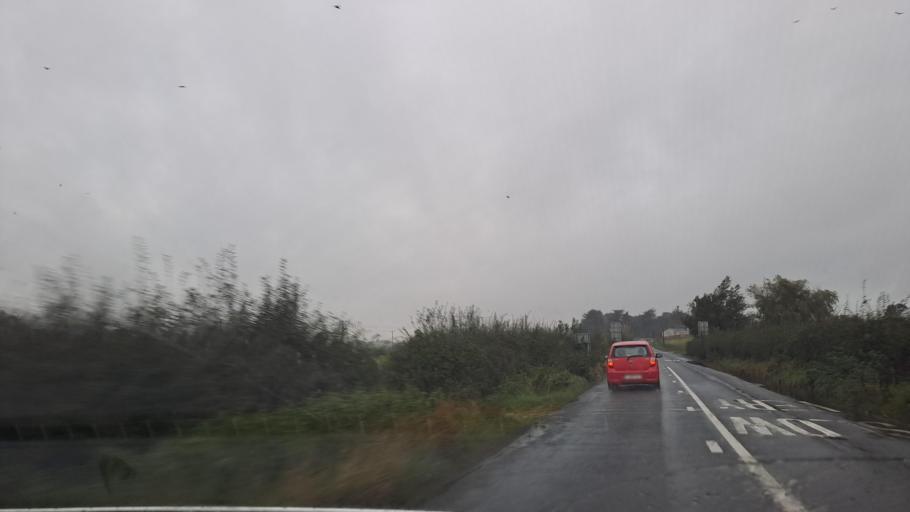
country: IE
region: Leinster
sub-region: Lu
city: Ardee
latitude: 53.9718
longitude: -6.5530
